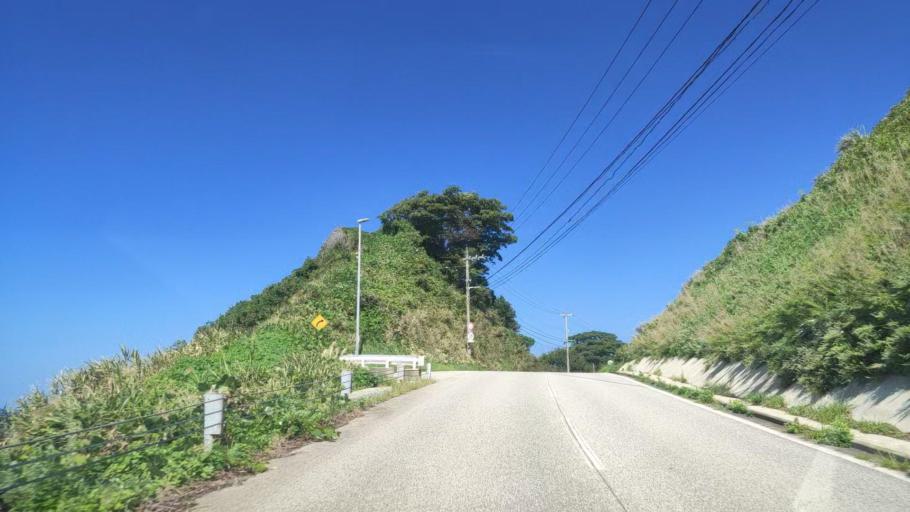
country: JP
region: Ishikawa
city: Nanao
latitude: 37.4472
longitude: 137.0480
